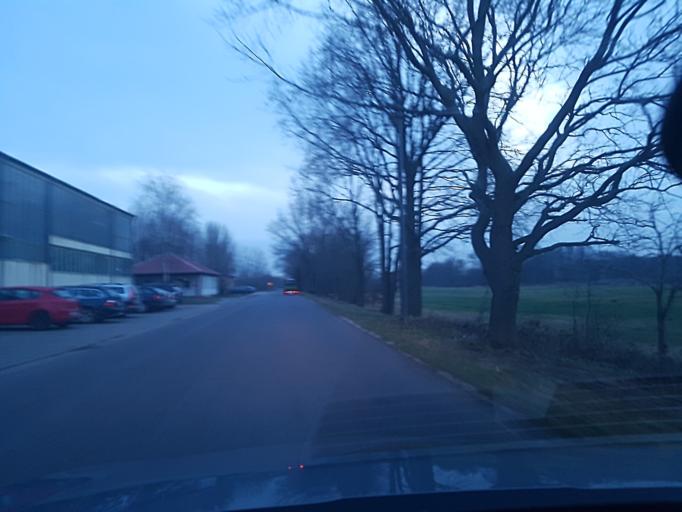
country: DE
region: Brandenburg
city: Doberlug-Kirchhain
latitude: 51.6042
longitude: 13.5470
